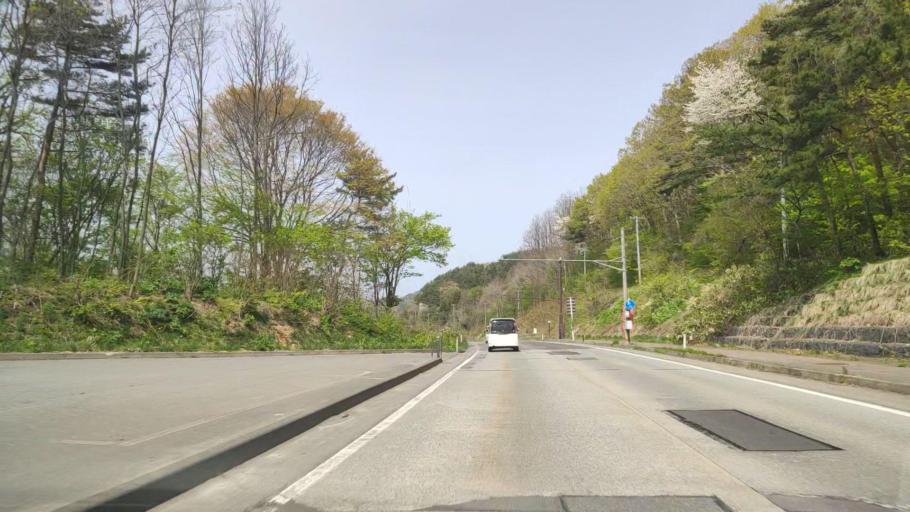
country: JP
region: Aomori
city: Aomori Shi
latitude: 40.8615
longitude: 140.8443
